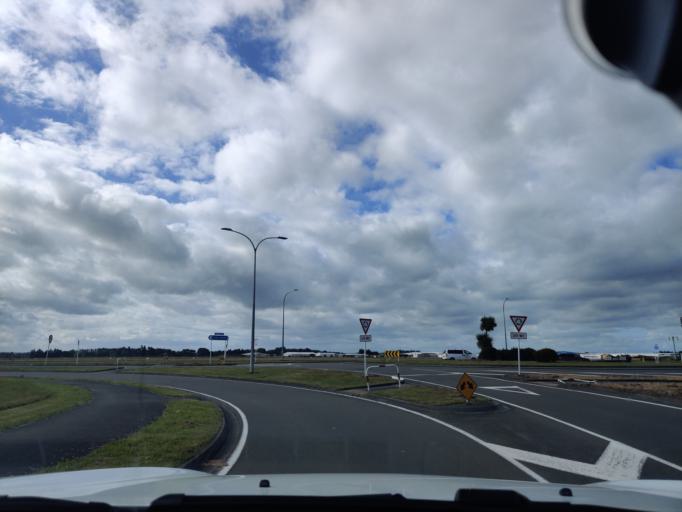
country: NZ
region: Manawatu-Wanganui
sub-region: Palmerston North City
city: Palmerston North
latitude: -40.3251
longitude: 175.6253
